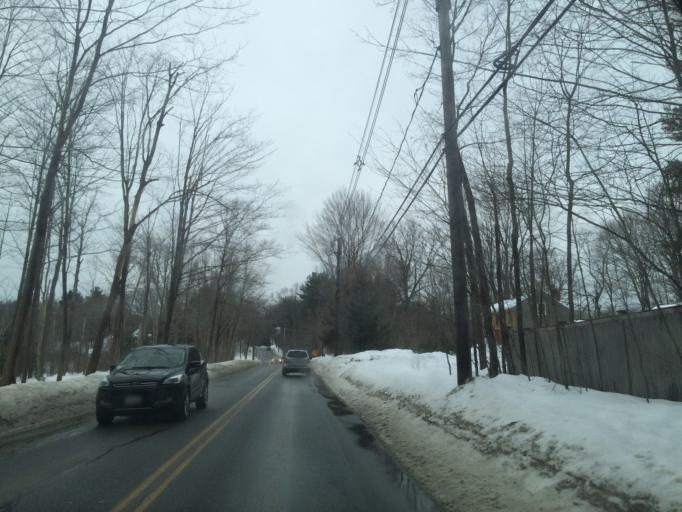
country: US
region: Massachusetts
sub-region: Middlesex County
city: Lincoln
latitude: 42.4235
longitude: -71.3375
